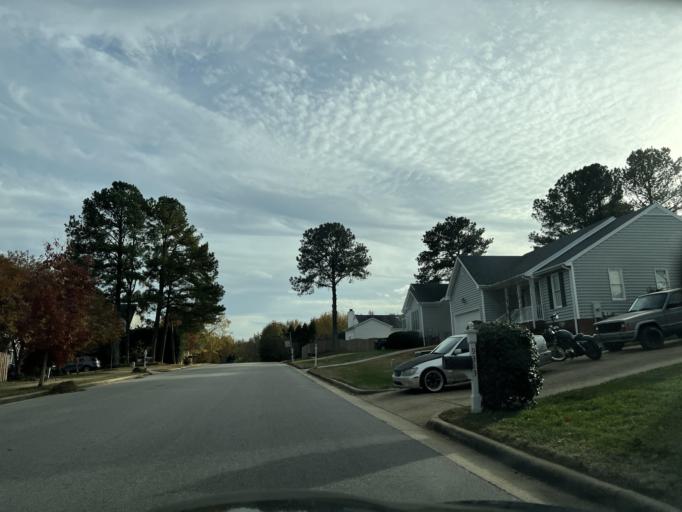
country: US
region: North Carolina
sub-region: Wake County
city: Wake Forest
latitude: 35.9042
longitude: -78.5941
